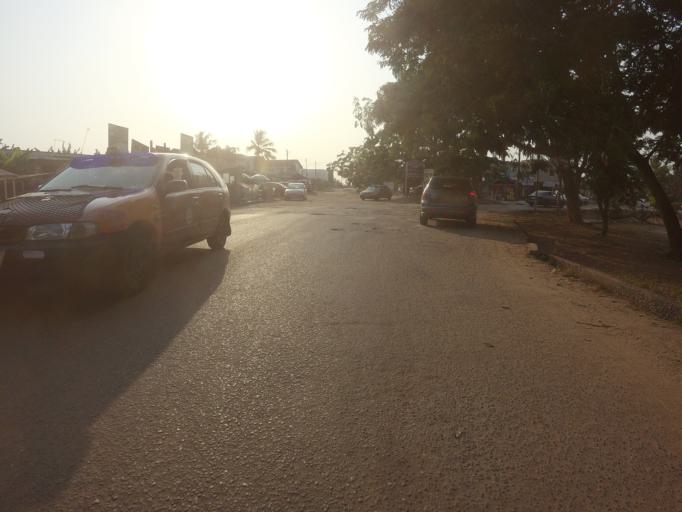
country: GH
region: Greater Accra
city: Nungua
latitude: 5.6162
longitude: -0.0516
